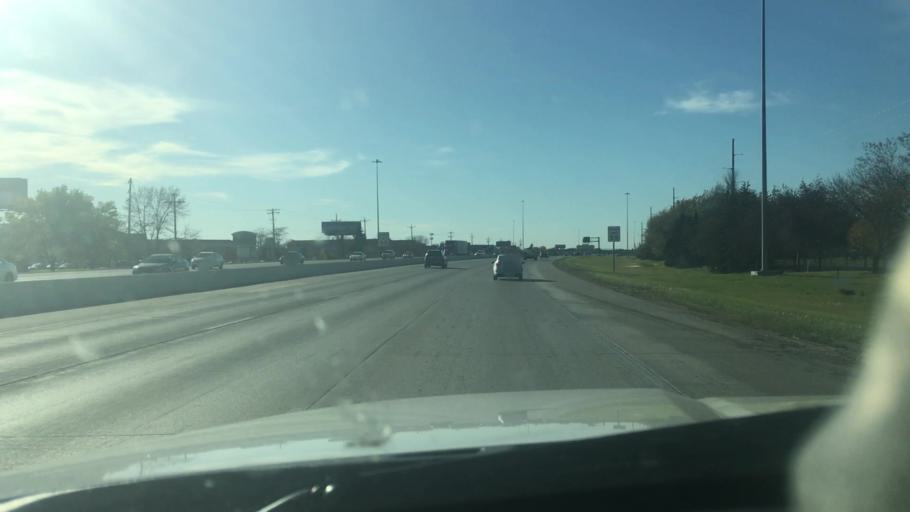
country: US
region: North Dakota
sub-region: Cass County
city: Fargo
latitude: 46.8477
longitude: -96.8076
